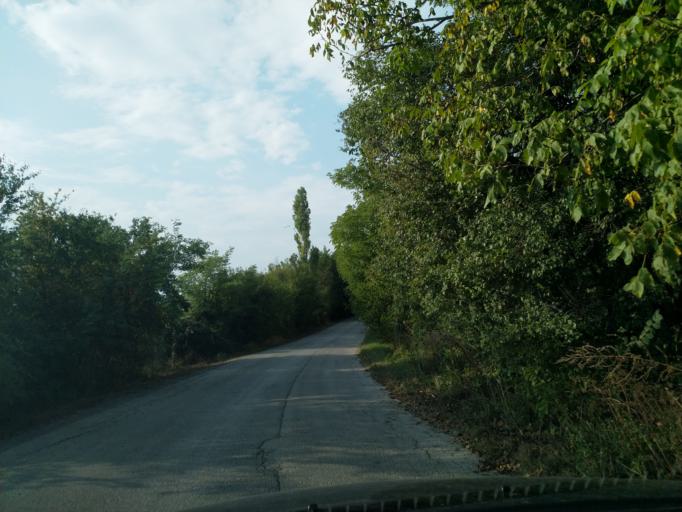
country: RS
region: Central Serbia
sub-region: Pomoravski Okrug
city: Paracin
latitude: 43.8447
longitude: 21.5277
